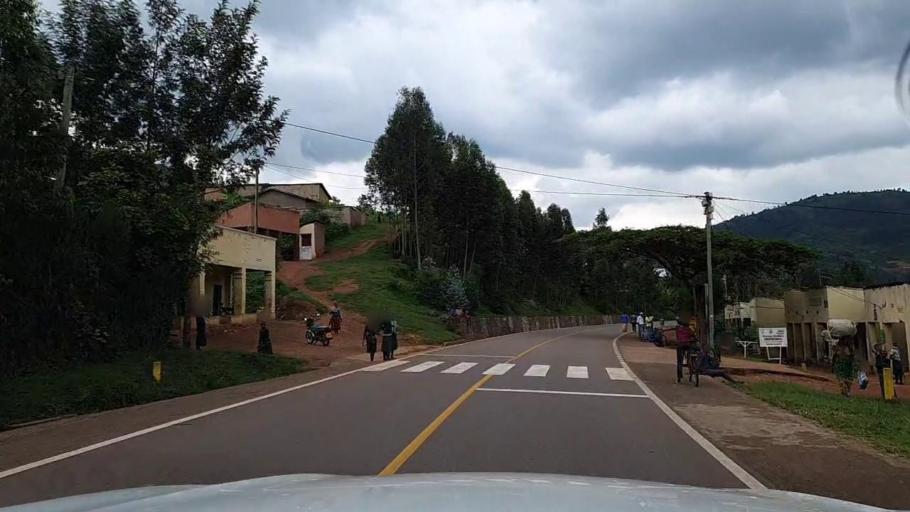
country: RW
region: Northern Province
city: Byumba
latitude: -1.6805
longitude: 30.1013
